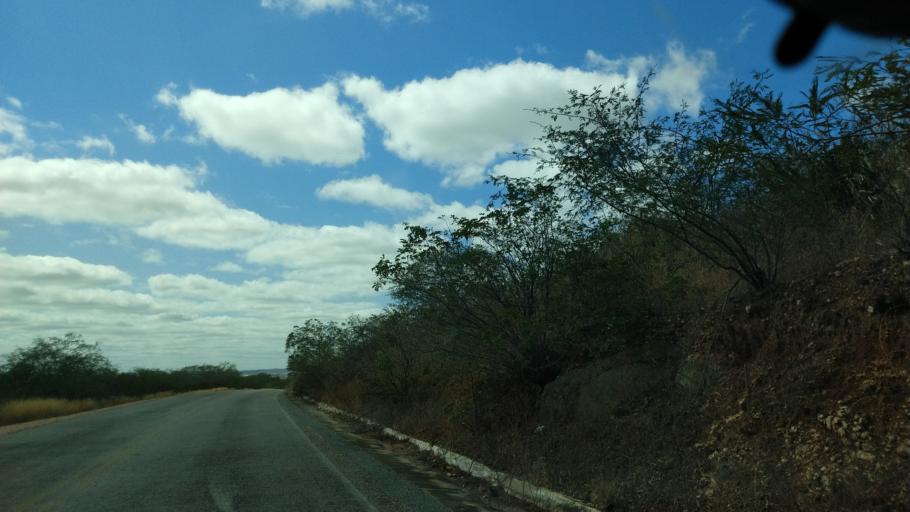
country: BR
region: Rio Grande do Norte
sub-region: Currais Novos
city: Currais Novos
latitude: -6.2609
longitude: -36.5749
